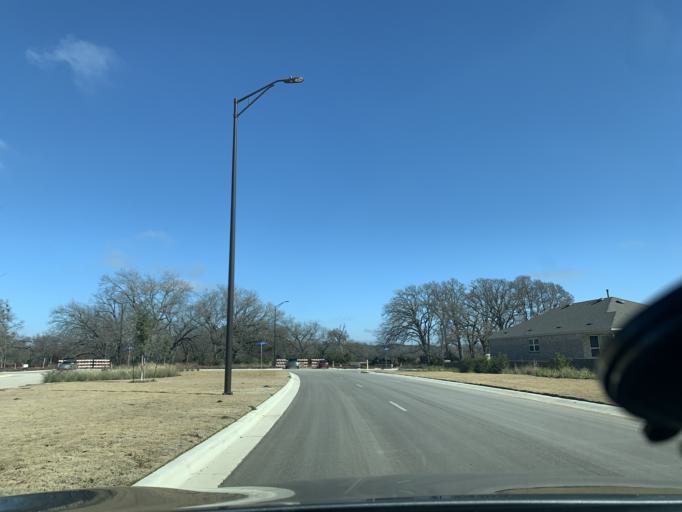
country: US
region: Texas
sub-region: Williamson County
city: Serenada
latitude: 30.7321
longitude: -97.7558
